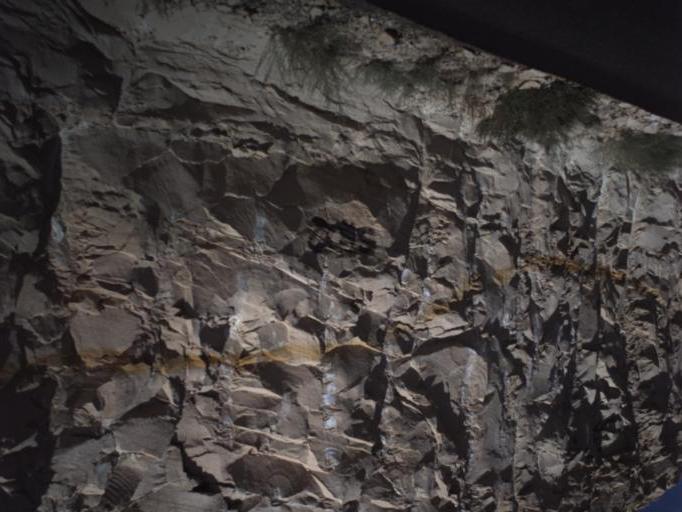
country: US
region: Utah
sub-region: Wayne County
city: Loa
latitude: 37.8164
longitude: -111.4104
